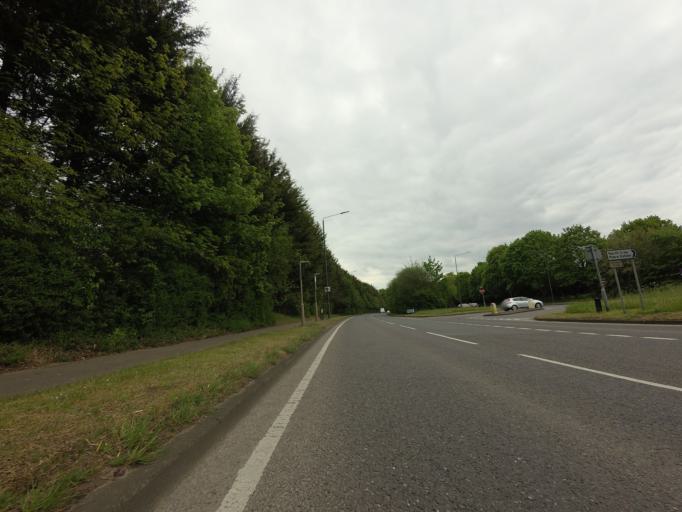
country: GB
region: England
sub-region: Greater London
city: Bexley
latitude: 51.4227
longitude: 0.1343
